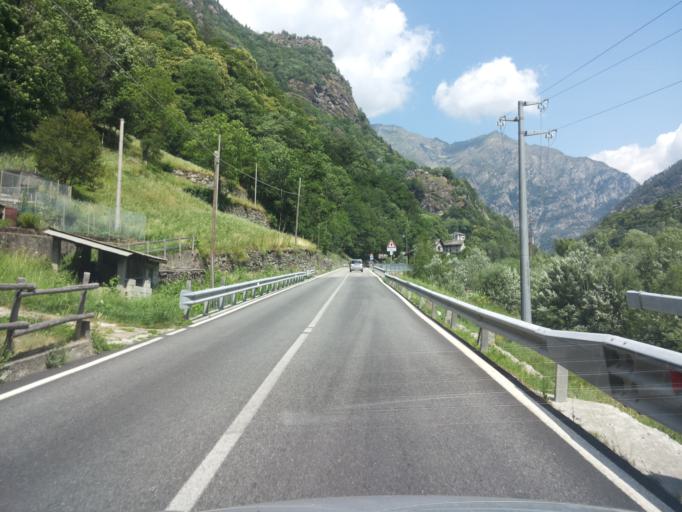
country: IT
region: Aosta Valley
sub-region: Valle d'Aosta
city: Fontainemore
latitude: 45.6578
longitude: 7.8589
